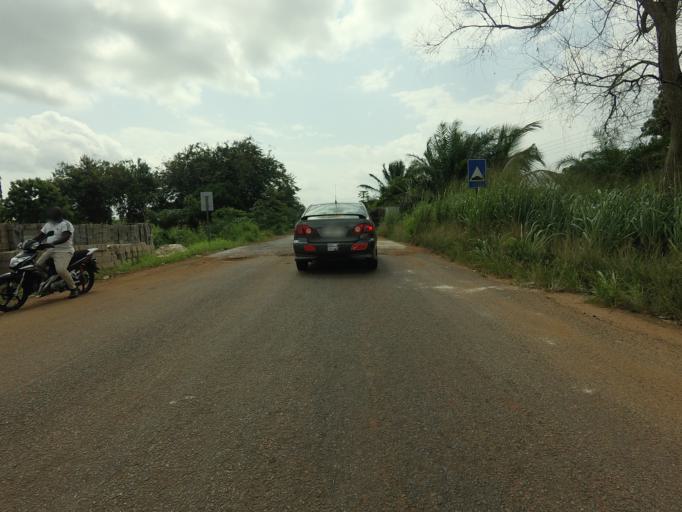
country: TG
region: Maritime
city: Lome
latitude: 6.2187
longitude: 1.0451
